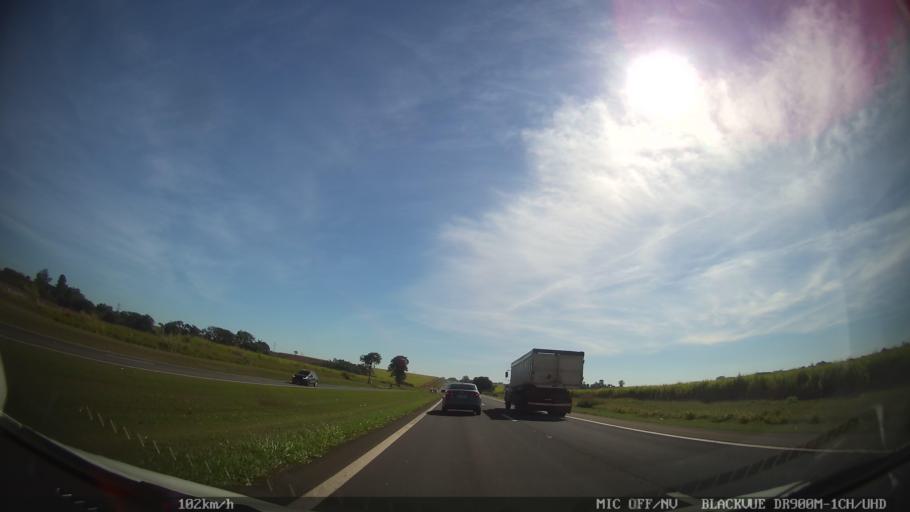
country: BR
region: Sao Paulo
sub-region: Leme
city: Leme
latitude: -22.1198
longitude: -47.4111
